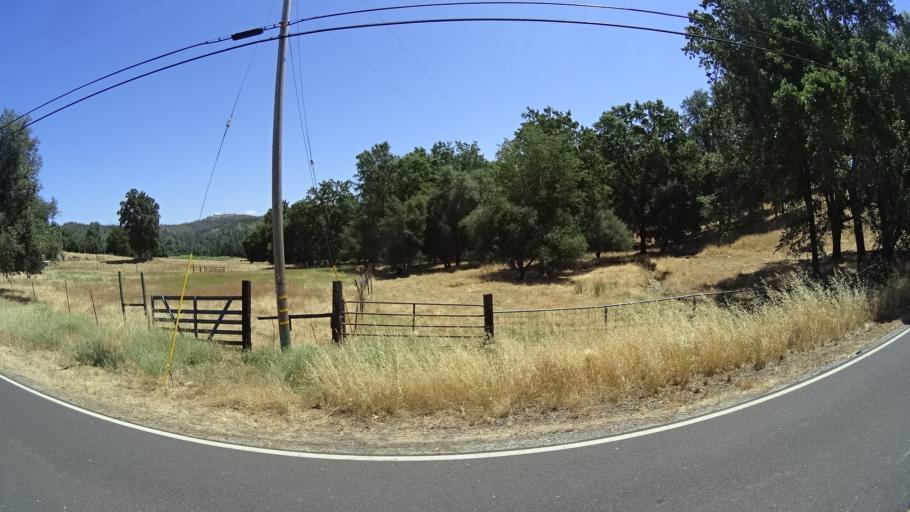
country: US
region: California
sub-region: Calaveras County
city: Mountain Ranch
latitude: 38.2187
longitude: -120.5430
